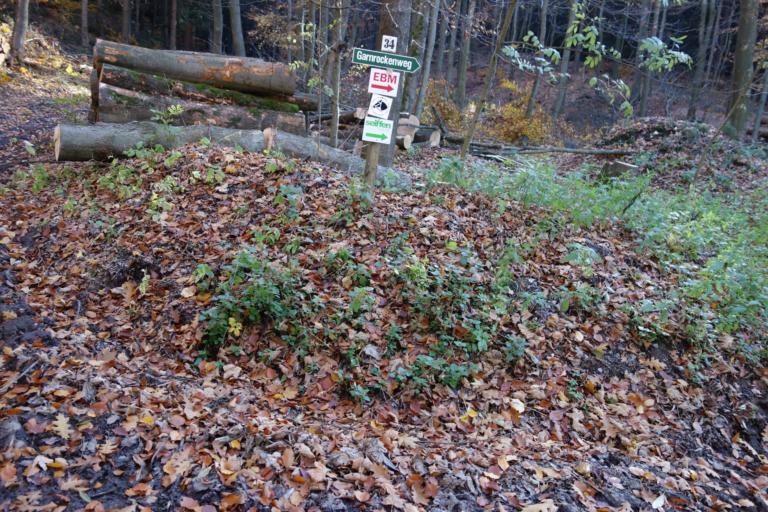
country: DE
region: Saxony
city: Seiffen
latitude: 50.6441
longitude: 13.4319
